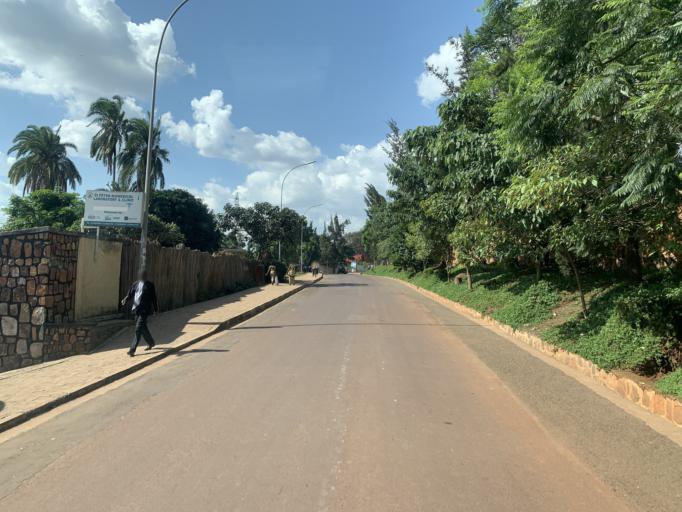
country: RW
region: Kigali
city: Kigali
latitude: -1.9591
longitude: 30.0605
